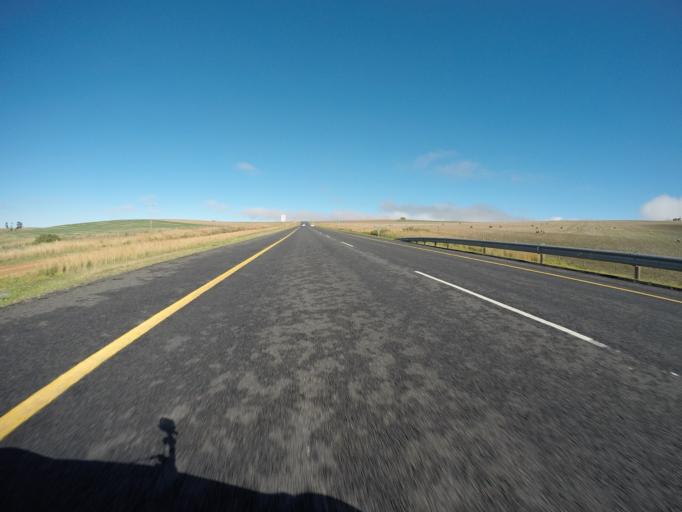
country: ZA
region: Western Cape
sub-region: Cape Winelands District Municipality
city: Ashton
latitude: -34.1308
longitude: 20.0313
